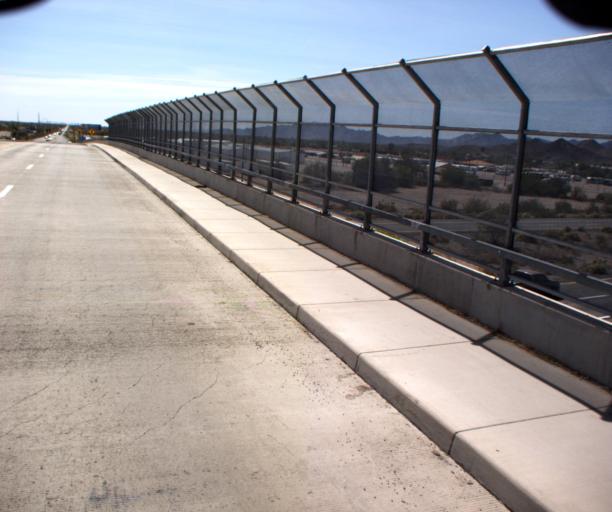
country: US
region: Arizona
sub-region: La Paz County
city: Quartzsite
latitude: 33.6635
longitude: -114.2172
